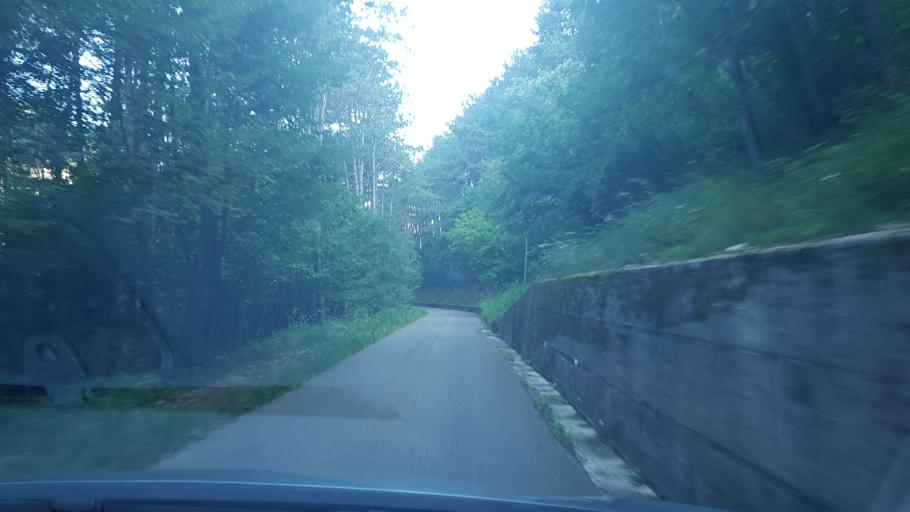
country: IT
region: Friuli Venezia Giulia
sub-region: Provincia di Udine
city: Moggio Udinese
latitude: 46.4316
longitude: 13.2053
